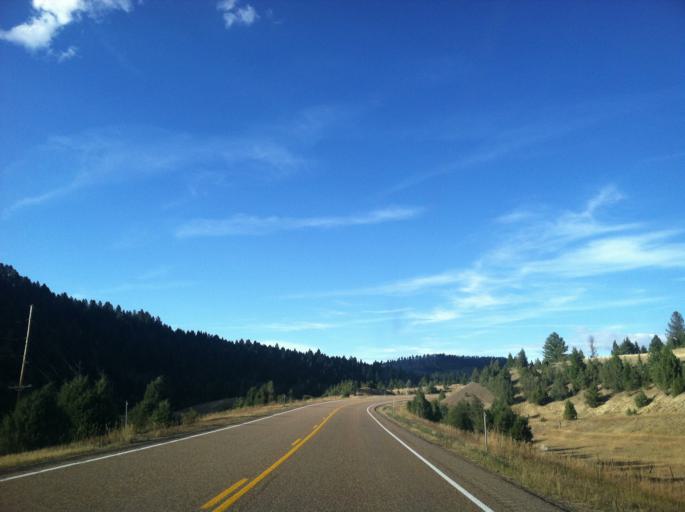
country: US
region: Montana
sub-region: Granite County
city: Philipsburg
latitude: 46.3958
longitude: -113.3080
